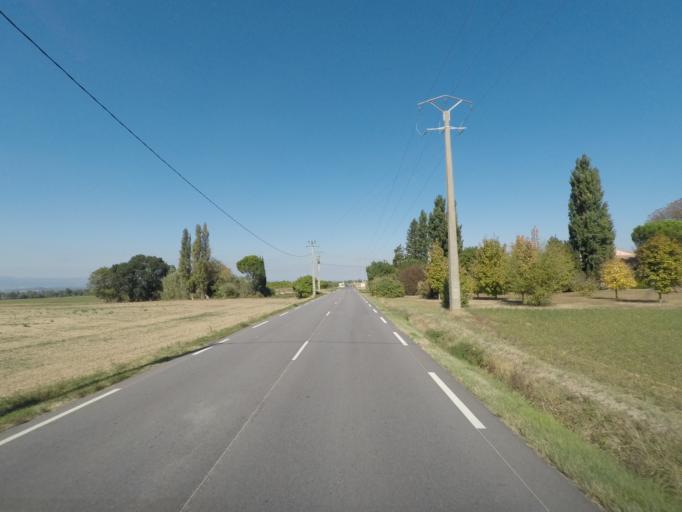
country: FR
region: Rhone-Alpes
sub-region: Departement de la Drome
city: Upie
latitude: 44.7985
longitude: 5.0173
